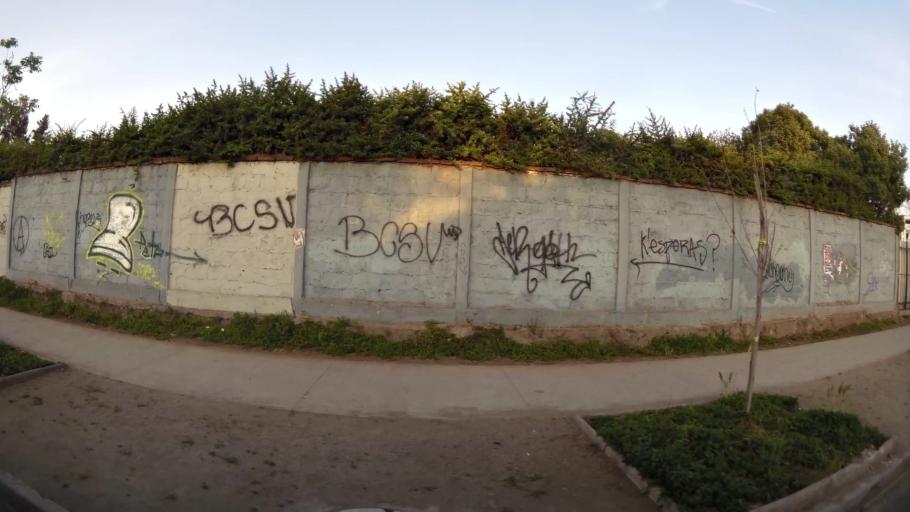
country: CL
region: Santiago Metropolitan
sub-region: Provincia de Cordillera
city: Puente Alto
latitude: -33.6006
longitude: -70.5883
